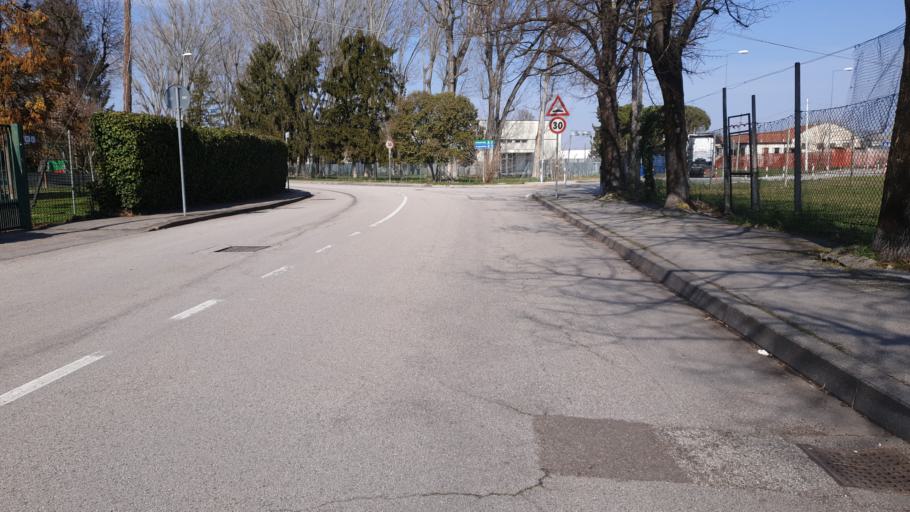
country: IT
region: Veneto
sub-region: Provincia di Padova
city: Cadoneghe
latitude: 45.4160
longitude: 11.9164
